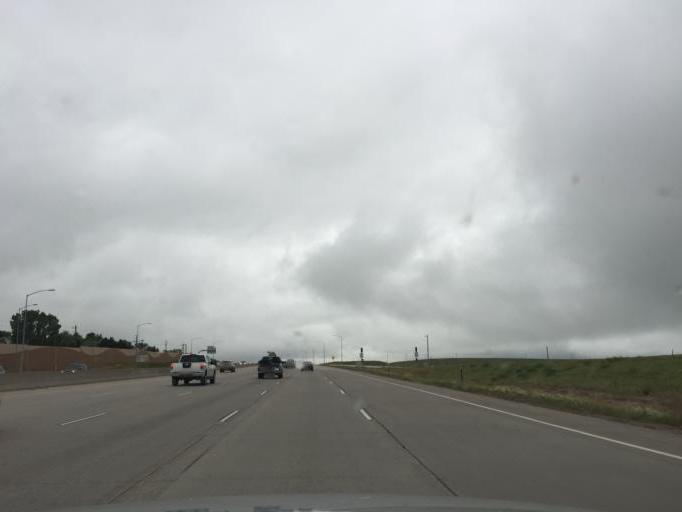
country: US
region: Colorado
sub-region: Park County
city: Castle Pines North
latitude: 39.4728
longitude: -104.8724
